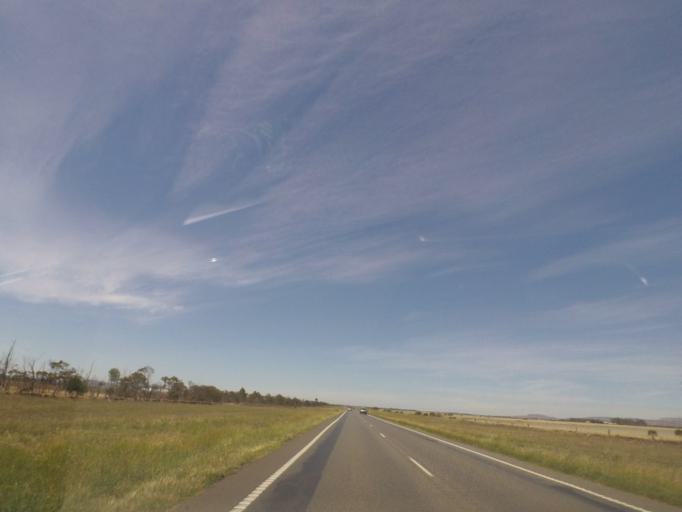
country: AU
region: Victoria
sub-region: Wyndham
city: Wyndham Vale
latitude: -37.8190
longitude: 144.3976
